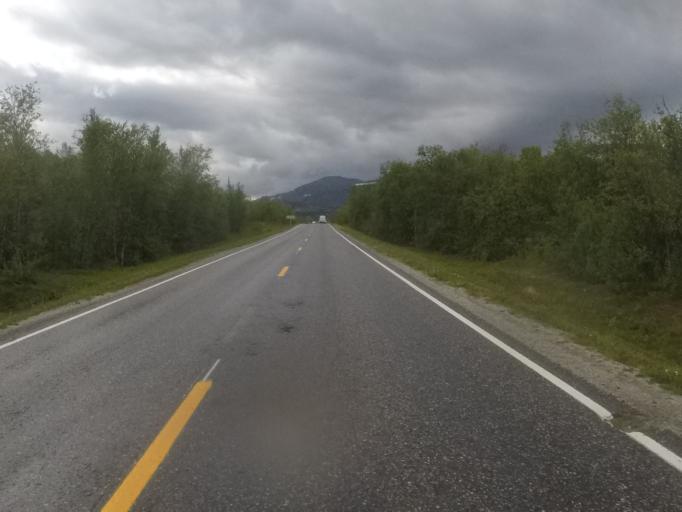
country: NO
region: Finnmark Fylke
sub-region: Porsanger
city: Lakselv
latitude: 69.9606
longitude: 24.9620
